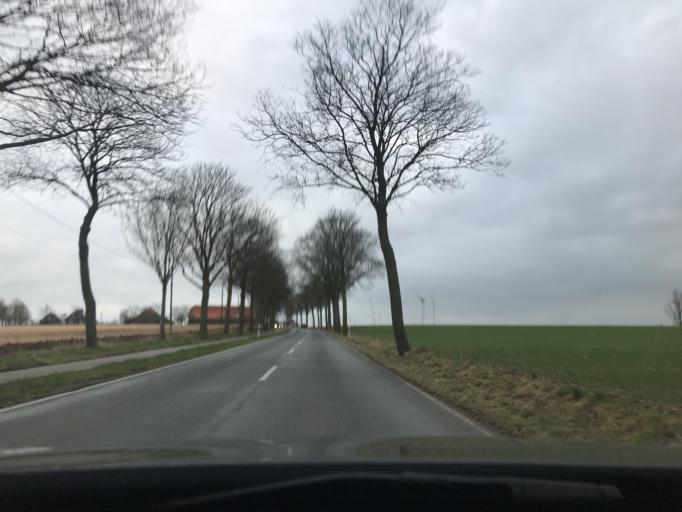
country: DE
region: North Rhine-Westphalia
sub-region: Regierungsbezirk Dusseldorf
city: Goch
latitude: 51.7275
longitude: 6.2101
